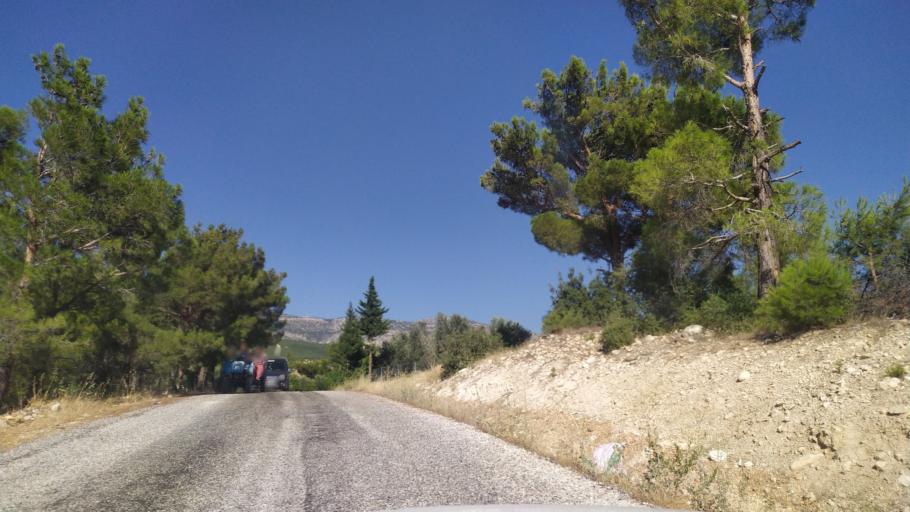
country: TR
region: Mersin
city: Mut
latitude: 36.7023
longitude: 33.4746
